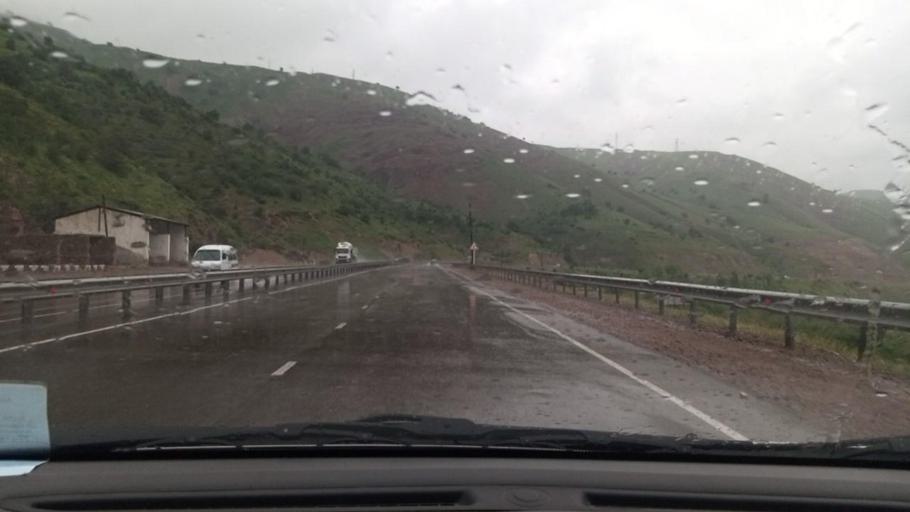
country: UZ
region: Toshkent
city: Angren
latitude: 41.0893
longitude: 70.3211
